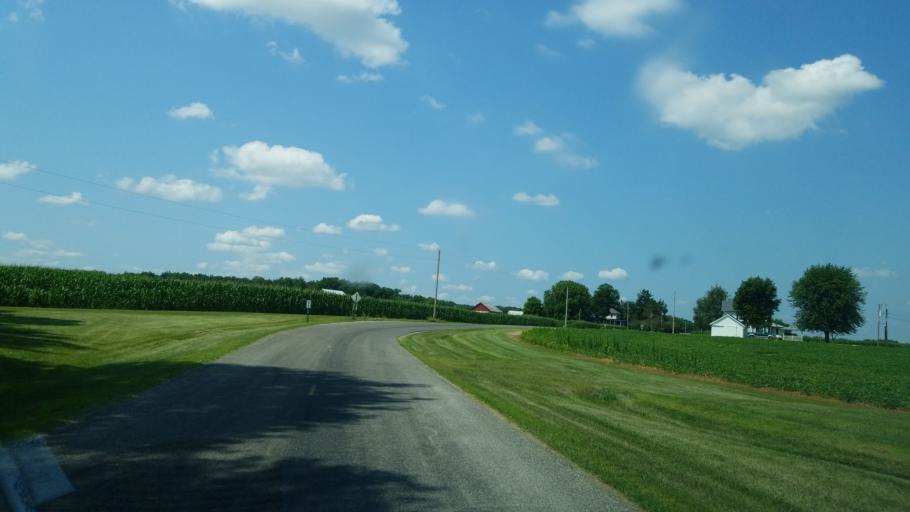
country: US
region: Ohio
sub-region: Delaware County
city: Ashley
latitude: 40.3490
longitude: -82.8943
